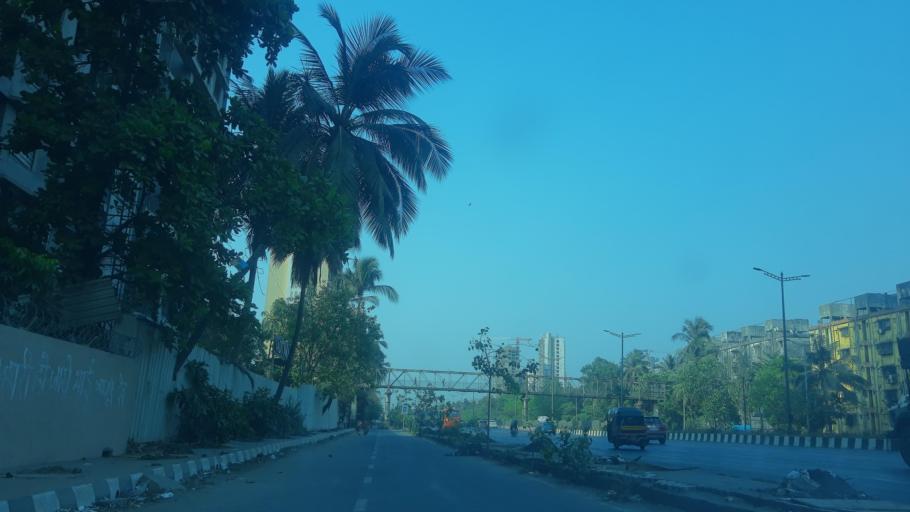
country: IN
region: Maharashtra
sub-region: Mumbai Suburban
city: Powai
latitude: 19.1150
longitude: 72.9346
